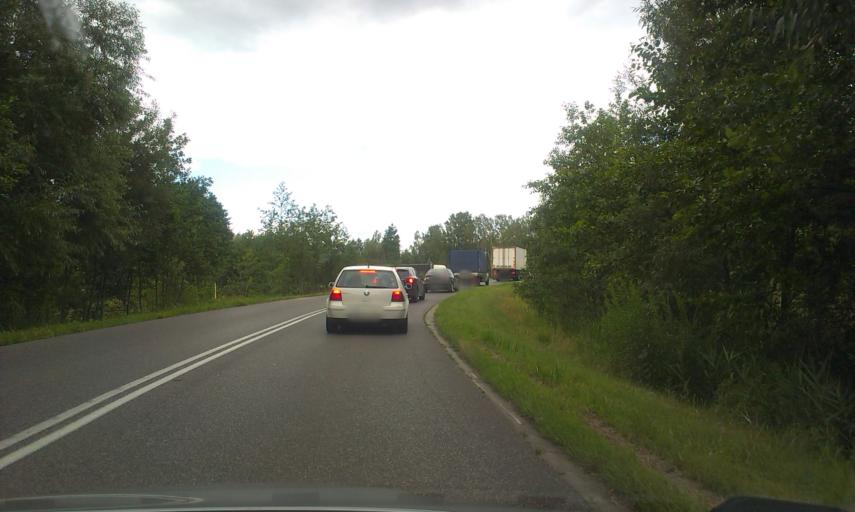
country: PL
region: Masovian Voivodeship
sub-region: Powiat zyrardowski
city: Mszczonow
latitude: 51.9923
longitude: 20.5018
